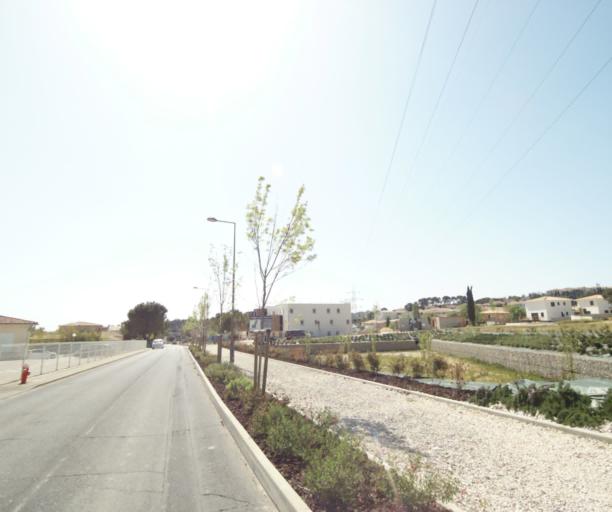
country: FR
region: Languedoc-Roussillon
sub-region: Departement de l'Herault
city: Montferrier-sur-Lez
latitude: 43.6509
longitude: 3.8347
